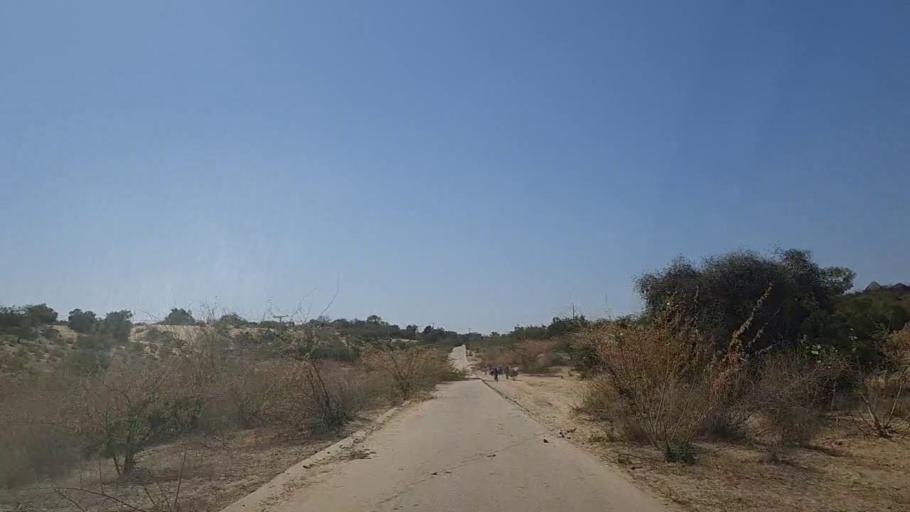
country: PK
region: Sindh
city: Mithi
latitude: 24.8264
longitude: 69.6803
